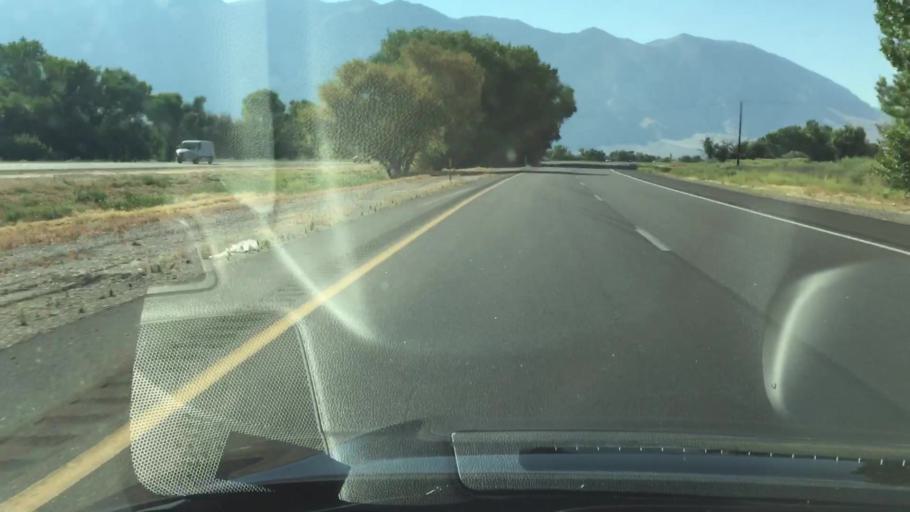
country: US
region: California
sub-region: Inyo County
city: West Bishop
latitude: 37.4067
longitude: -118.5450
